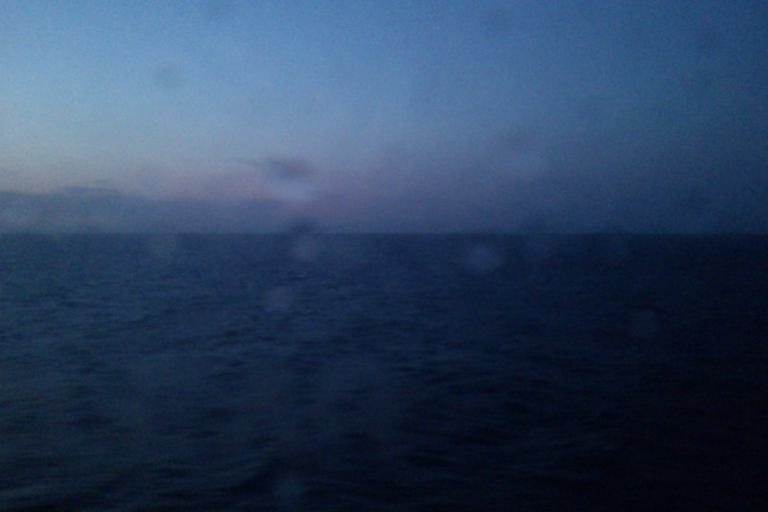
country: JP
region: Ishikawa
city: Kanazawa-shi
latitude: 37.0313
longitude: 135.9912
